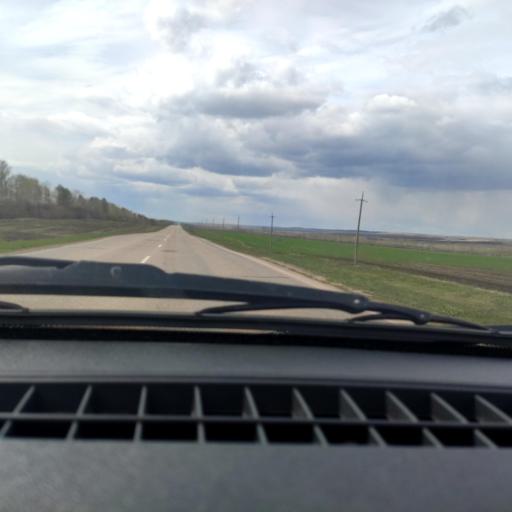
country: RU
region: Bashkortostan
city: Chekmagush
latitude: 55.1082
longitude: 54.9658
